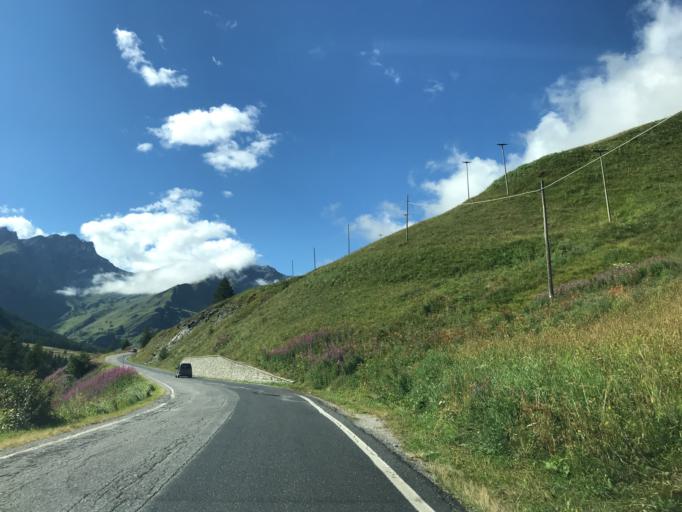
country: IT
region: Piedmont
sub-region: Provincia di Cuneo
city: Pontechianale
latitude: 44.6337
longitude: 7.0164
